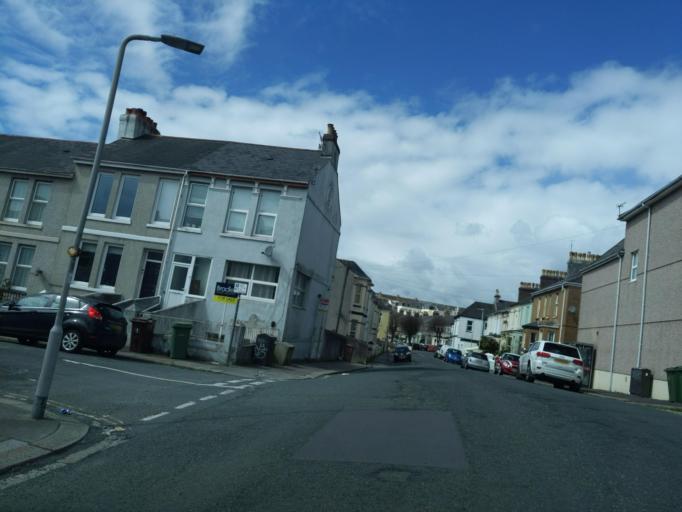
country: GB
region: England
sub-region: Plymouth
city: Plymouth
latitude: 50.3831
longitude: -4.1282
